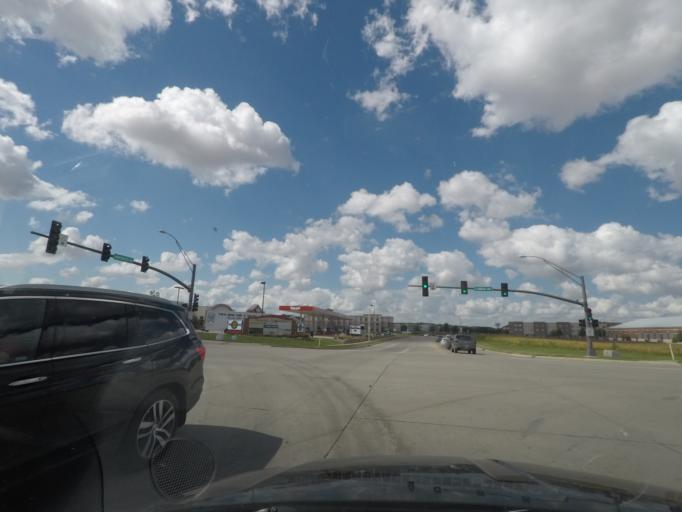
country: US
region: Iowa
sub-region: Story County
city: Ames
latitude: 42.0121
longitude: -93.6785
